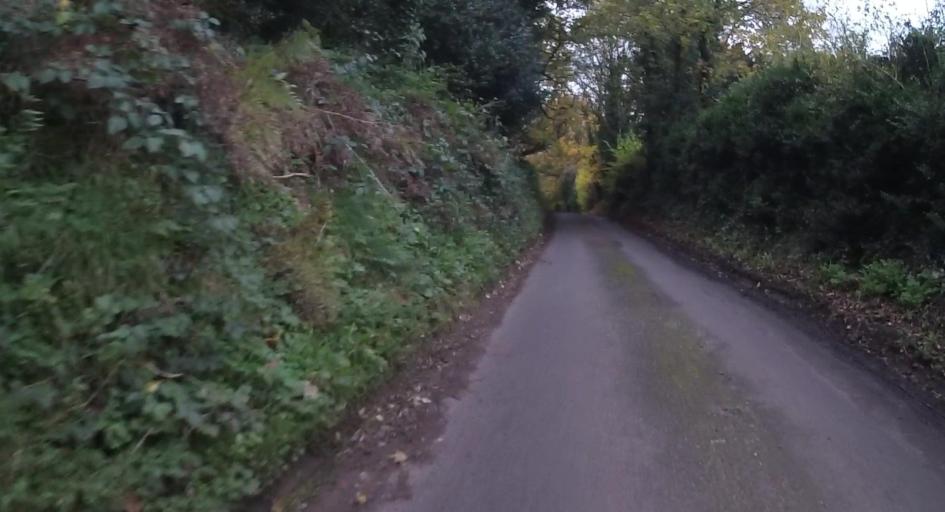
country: GB
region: England
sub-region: Hampshire
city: Lindford
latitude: 51.1331
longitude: -0.8238
